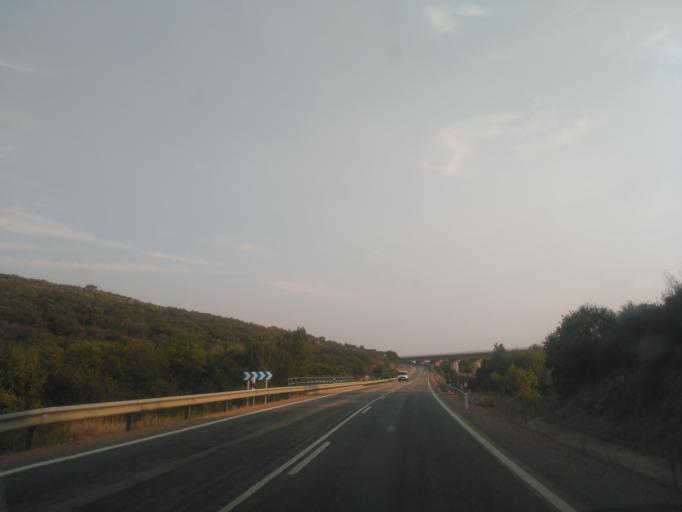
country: ES
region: Castille and Leon
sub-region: Provincia de Zamora
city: Perilla de Castro
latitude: 41.7539
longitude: -5.8548
